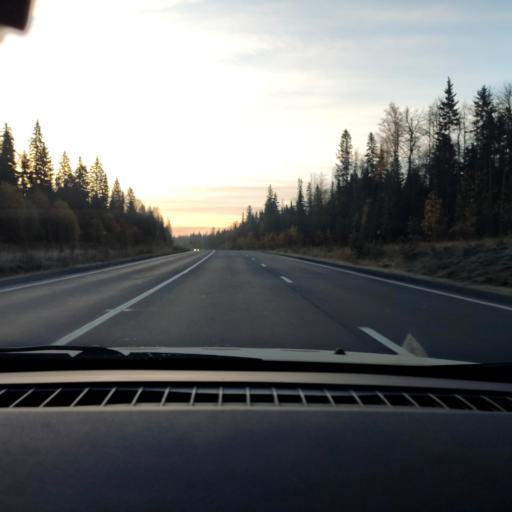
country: RU
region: Perm
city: Novyye Lyady
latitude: 58.0329
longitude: 56.4796
